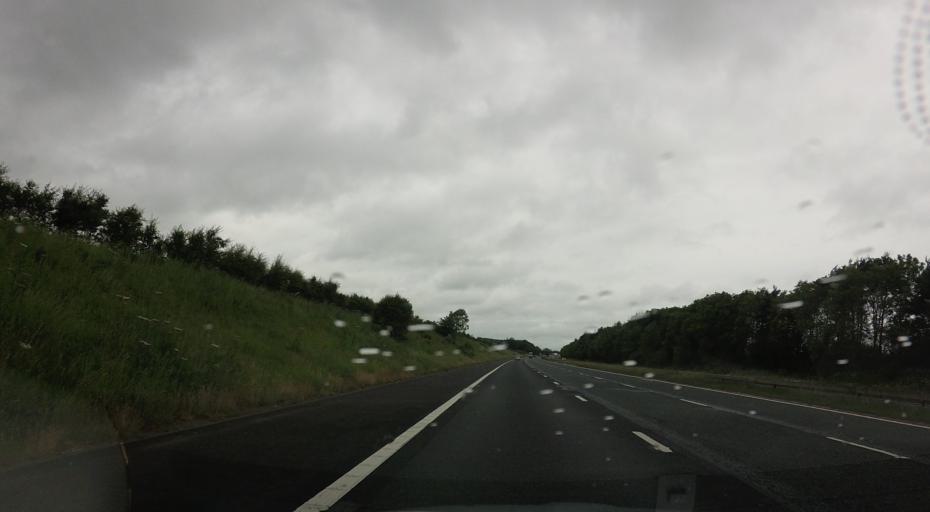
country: GB
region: England
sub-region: Cumbria
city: Penrith
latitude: 54.7165
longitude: -2.7977
